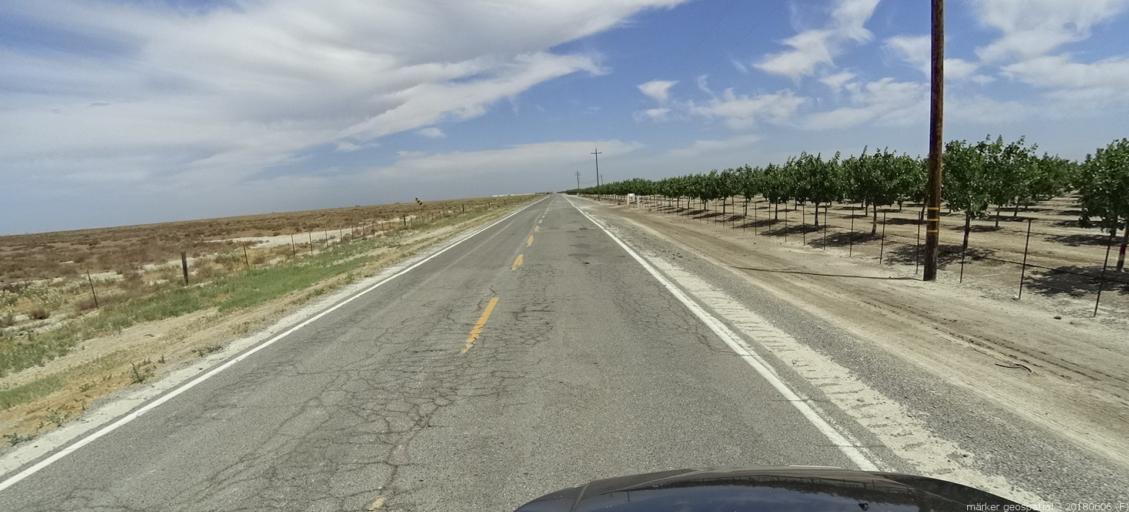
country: US
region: California
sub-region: Fresno County
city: Firebaugh
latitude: 36.8886
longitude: -120.3819
